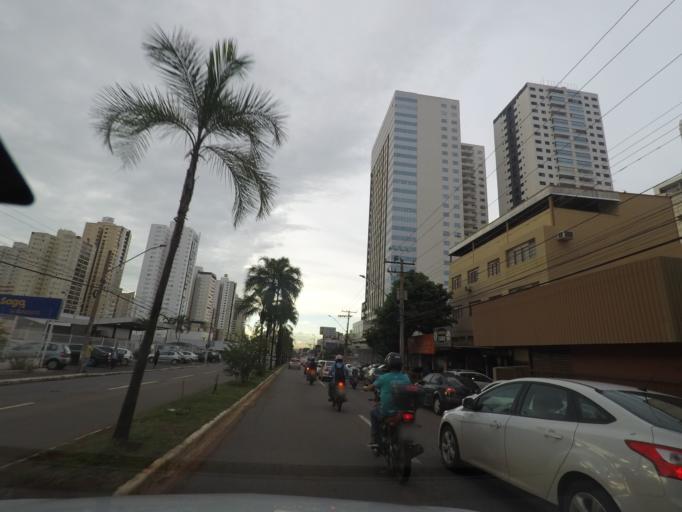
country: BR
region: Goias
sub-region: Goiania
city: Goiania
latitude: -16.6913
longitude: -49.2747
